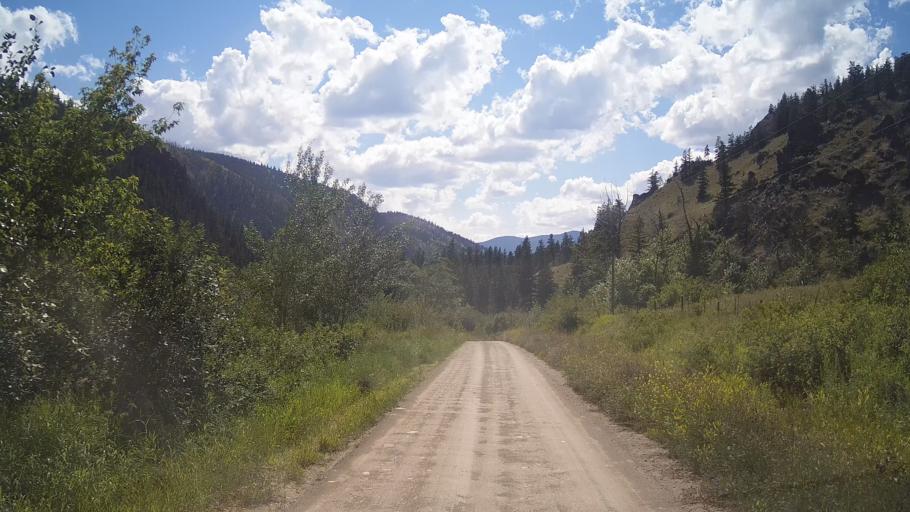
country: CA
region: British Columbia
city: Lillooet
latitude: 51.2363
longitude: -122.0494
